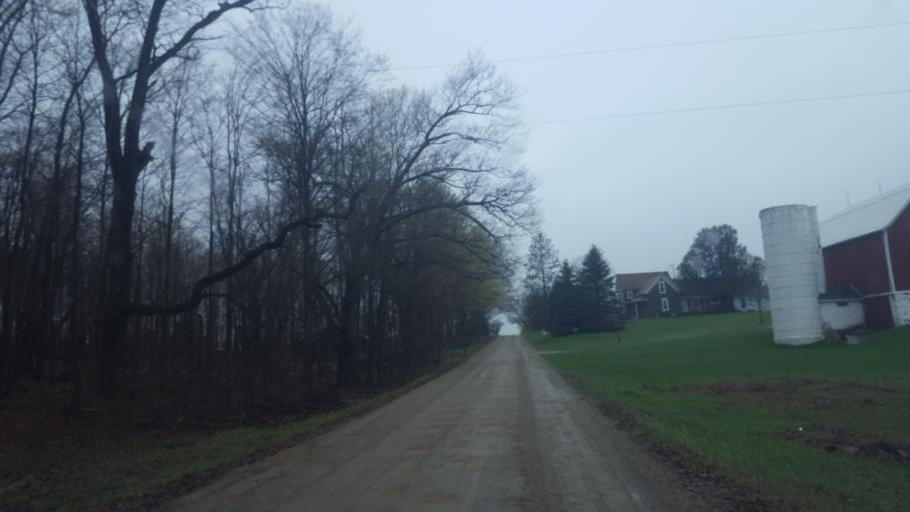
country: US
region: Michigan
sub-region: Isabella County
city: Lake Isabella
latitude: 43.5819
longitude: -84.9946
